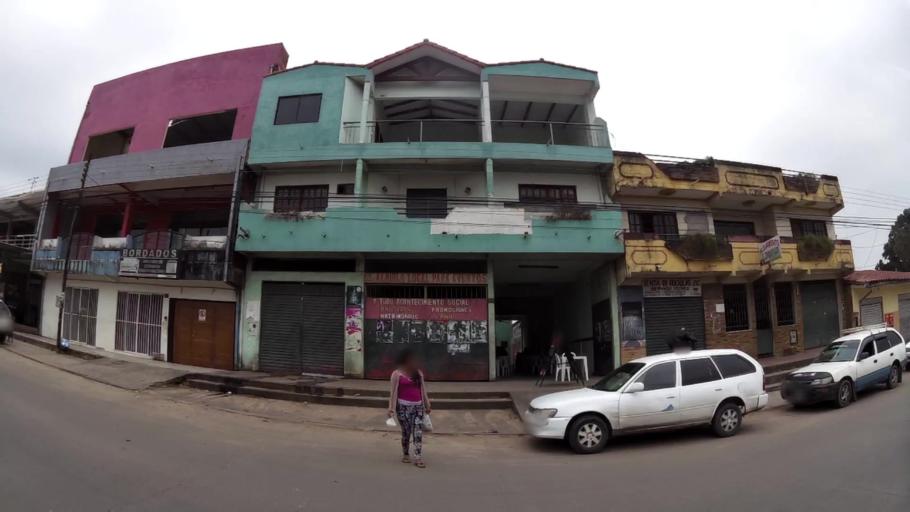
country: BO
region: Santa Cruz
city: Santa Cruz de la Sierra
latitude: -17.8321
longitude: -63.1816
